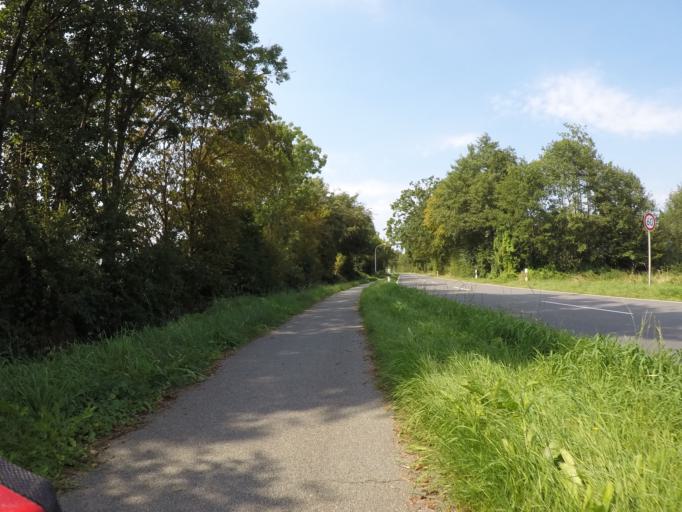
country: DE
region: Schleswig-Holstein
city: Winsen
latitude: 53.8395
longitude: 10.0355
